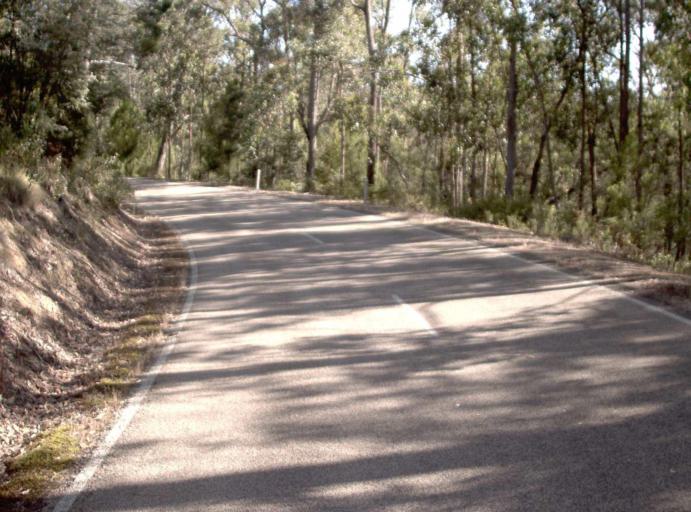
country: AU
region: Victoria
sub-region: East Gippsland
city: Lakes Entrance
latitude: -37.5646
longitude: 148.5589
